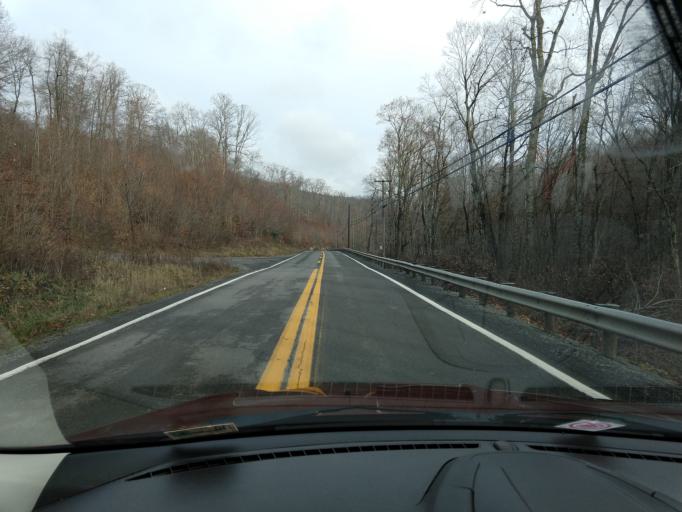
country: US
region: West Virginia
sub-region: Greenbrier County
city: Rainelle
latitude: 38.0861
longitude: -80.7077
